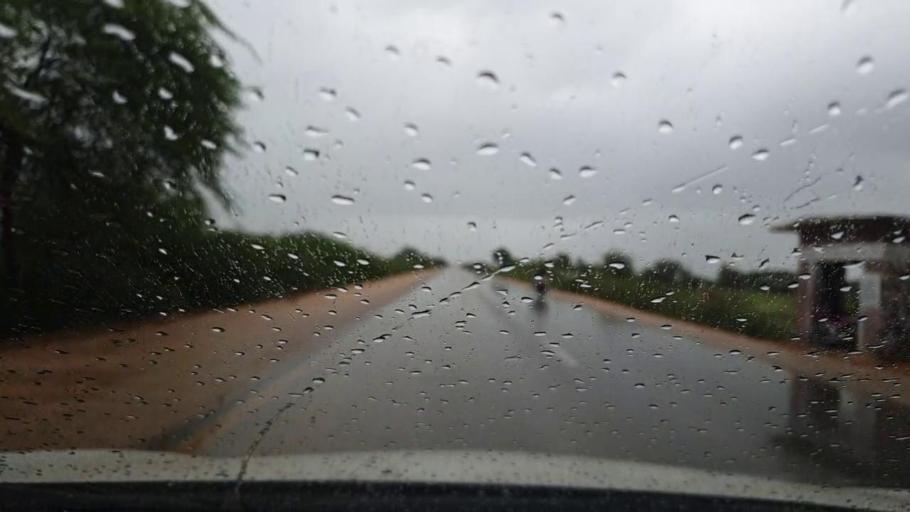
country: PK
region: Sindh
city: Kario
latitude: 24.6534
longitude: 68.5741
